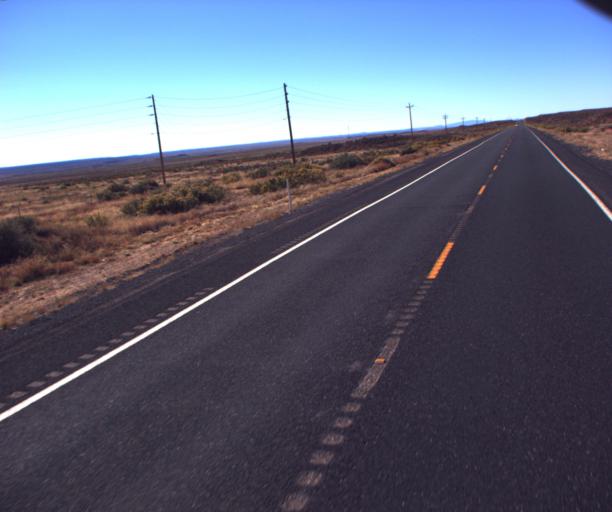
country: US
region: Arizona
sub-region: Coconino County
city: Fredonia
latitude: 36.9187
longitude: -112.5763
